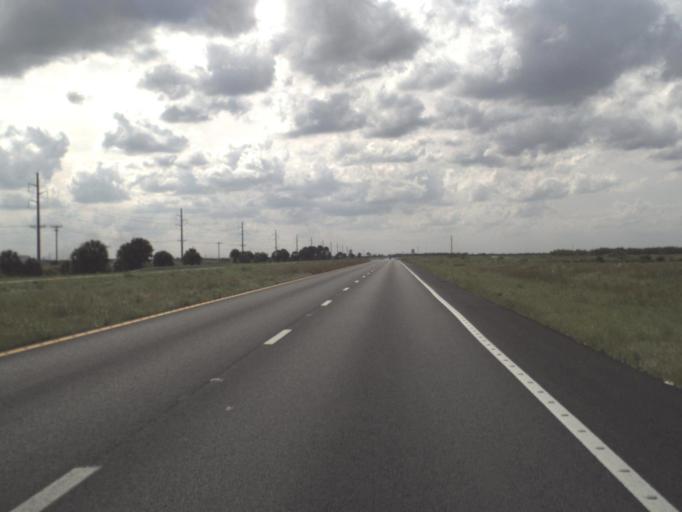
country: US
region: Florida
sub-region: Glades County
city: Moore Haven
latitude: 26.7535
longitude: -81.0946
